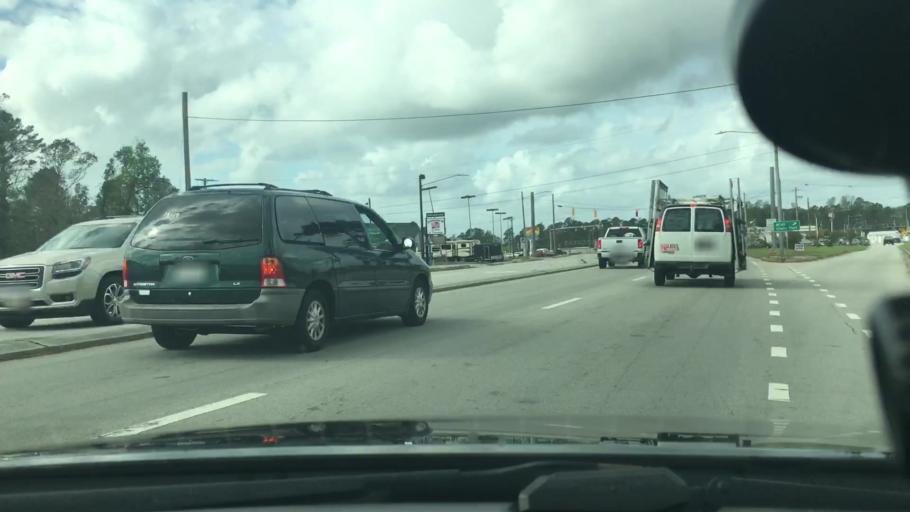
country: US
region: North Carolina
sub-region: Craven County
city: Havelock
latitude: 34.8783
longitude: -76.9049
